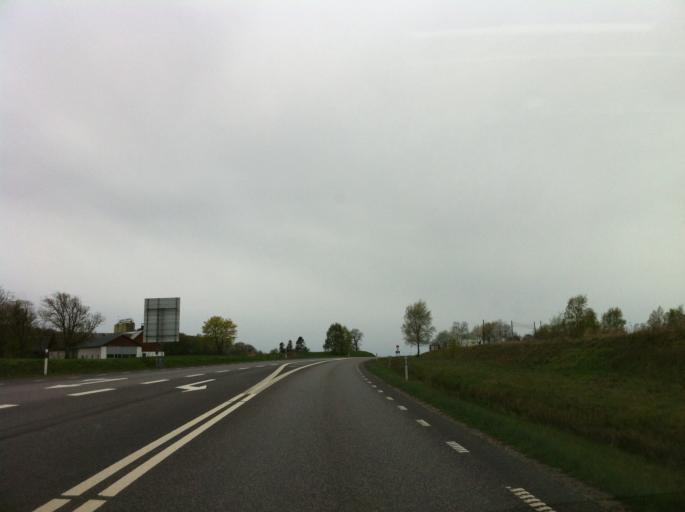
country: SE
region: Halland
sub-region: Falkenbergs Kommun
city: Falkenberg
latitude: 56.9594
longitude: 12.5556
